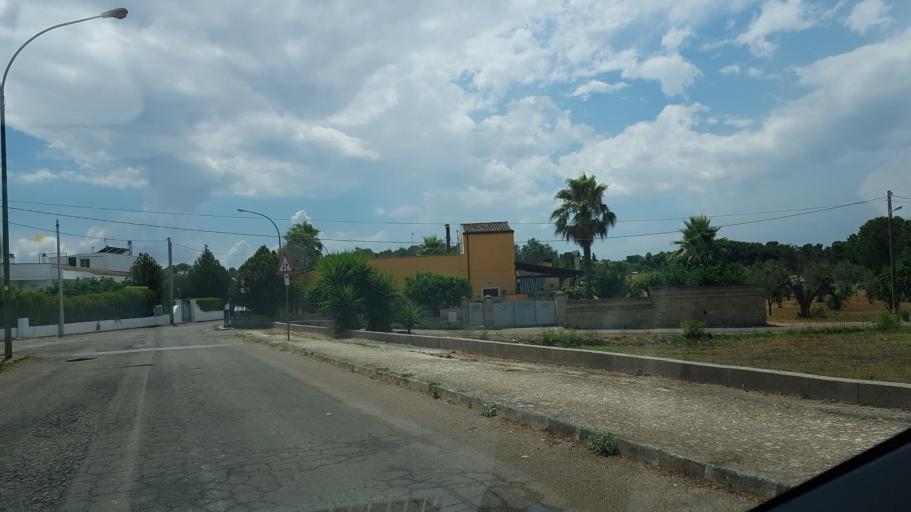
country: IT
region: Apulia
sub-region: Provincia di Lecce
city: Ruffano
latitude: 39.9670
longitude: 18.2609
